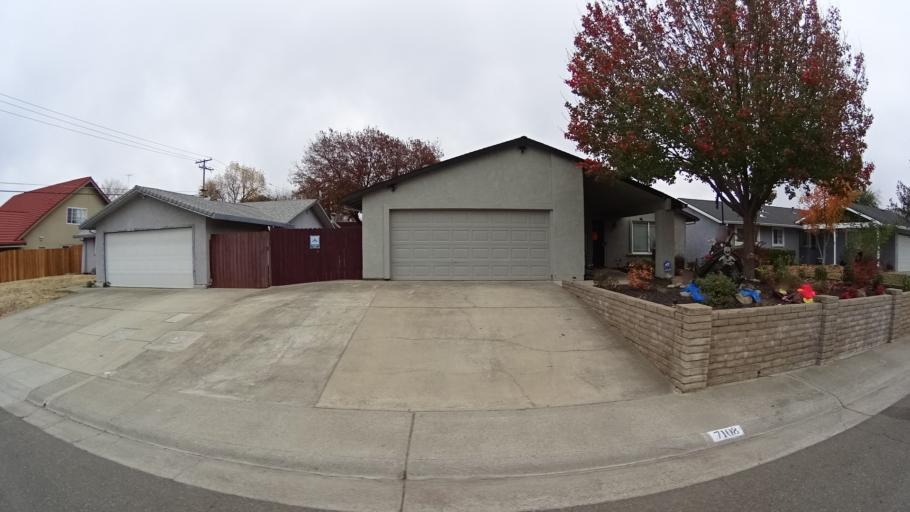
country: US
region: California
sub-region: Sacramento County
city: Antelope
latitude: 38.6949
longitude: -121.3078
